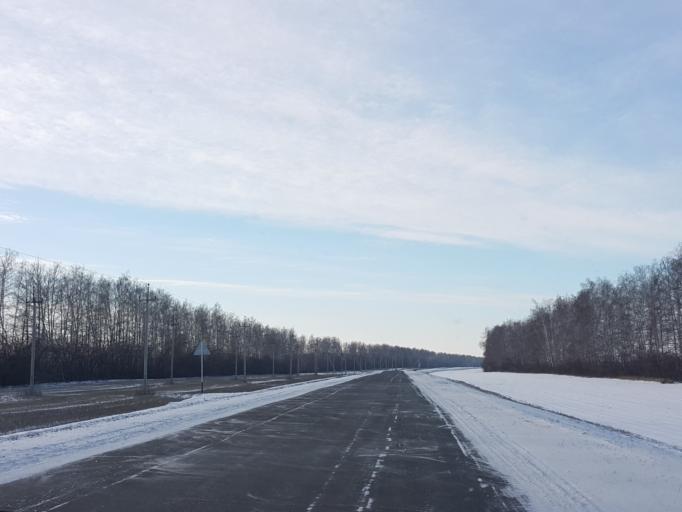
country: RU
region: Tambov
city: Znamenka
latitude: 52.3983
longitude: 41.3740
